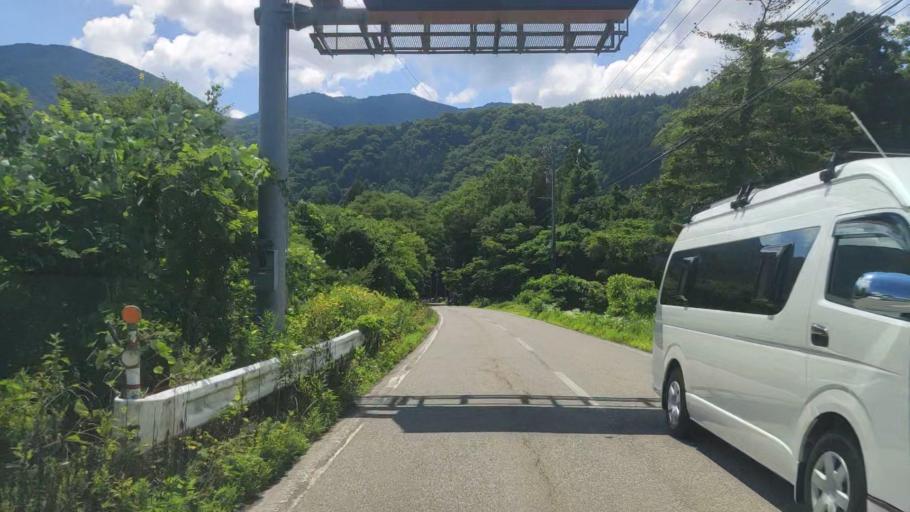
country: JP
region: Fukui
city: Ono
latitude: 35.9389
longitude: 136.5511
